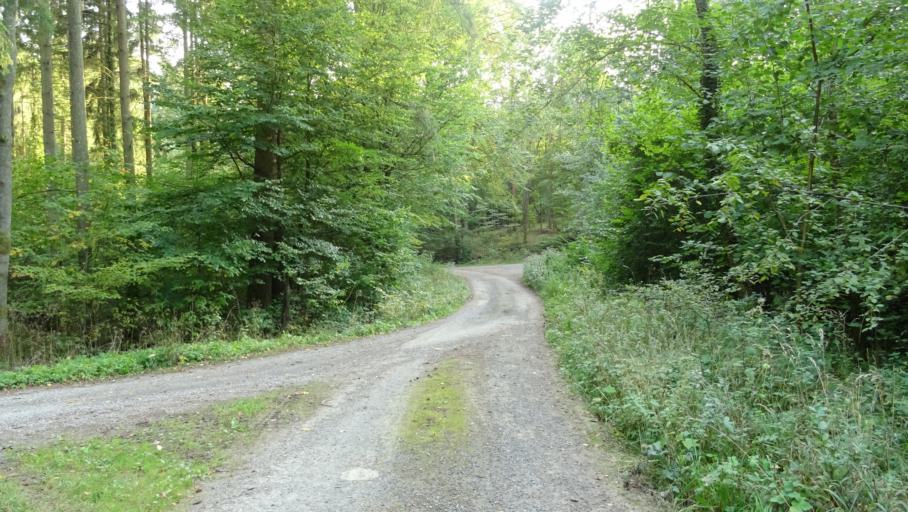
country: DE
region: Baden-Wuerttemberg
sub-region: Karlsruhe Region
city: Mosbach
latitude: 49.3918
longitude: 9.1631
